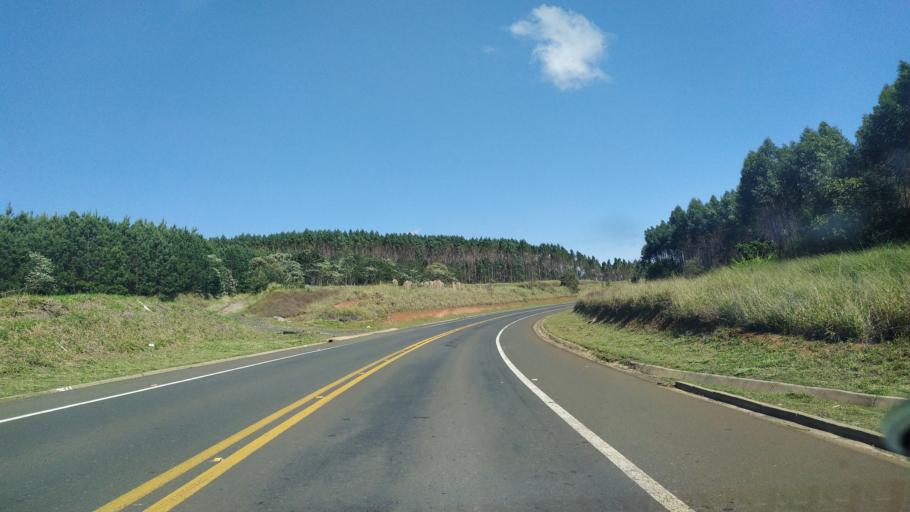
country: BR
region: Parana
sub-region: Telemaco Borba
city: Telemaco Borba
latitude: -24.2541
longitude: -50.7771
